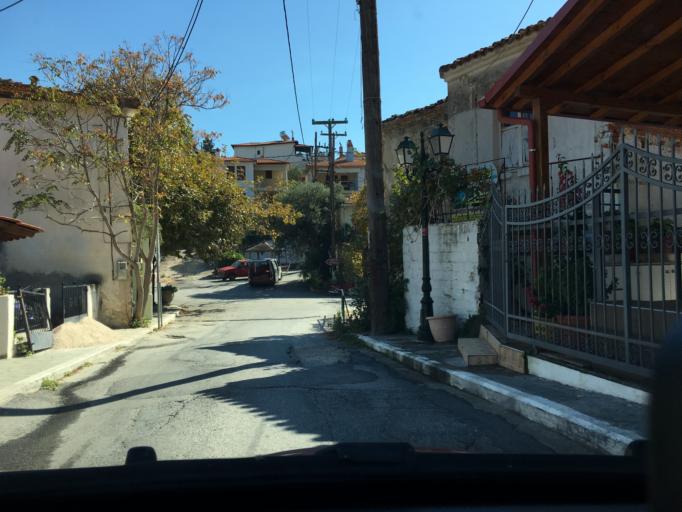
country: GR
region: Central Macedonia
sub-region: Nomos Chalkidikis
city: Agios Nikolaos
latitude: 40.3367
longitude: 23.7203
